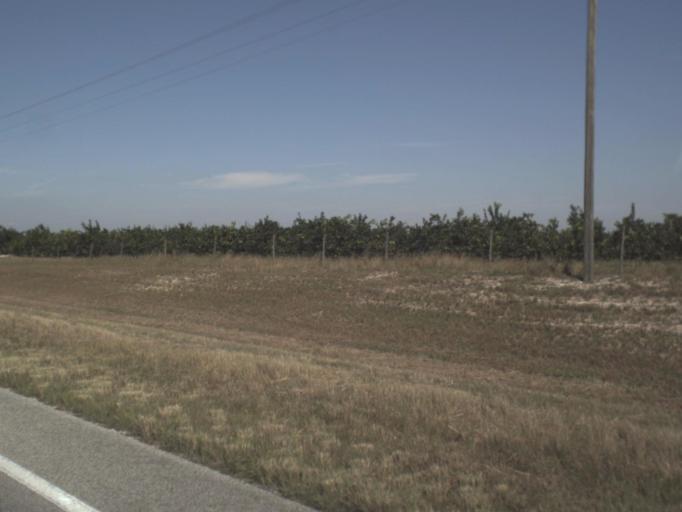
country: US
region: Florida
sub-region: Highlands County
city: Placid Lakes
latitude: 27.1515
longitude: -81.3286
